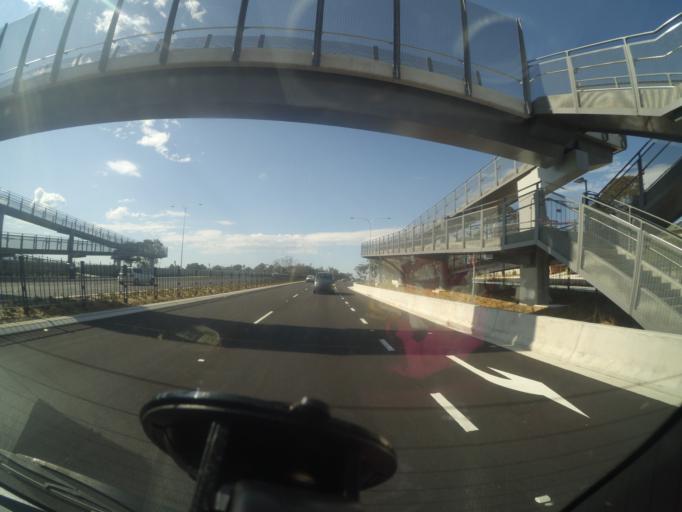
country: AU
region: New South Wales
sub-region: Blue Mountains Municipality
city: Lawson
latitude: -33.7236
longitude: 150.4156
